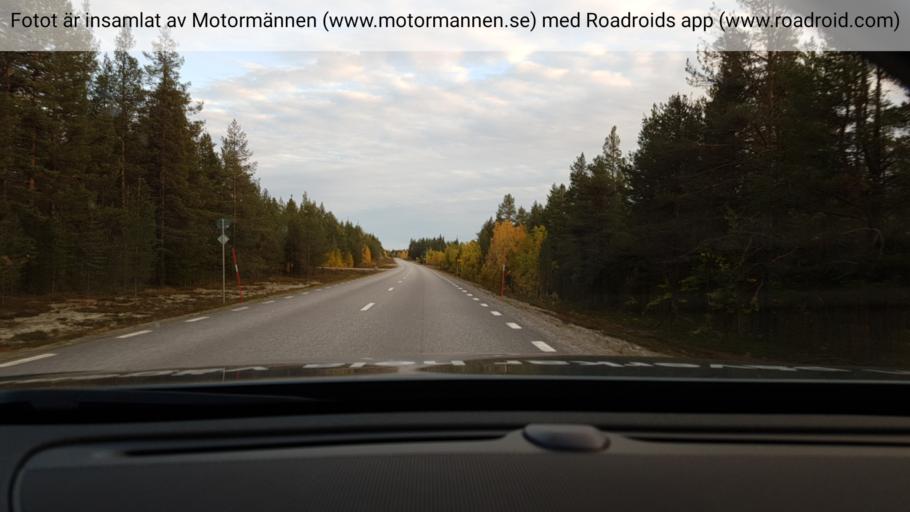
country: SE
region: Norrbotten
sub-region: Jokkmokks Kommun
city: Jokkmokk
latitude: 66.3926
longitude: 19.7011
